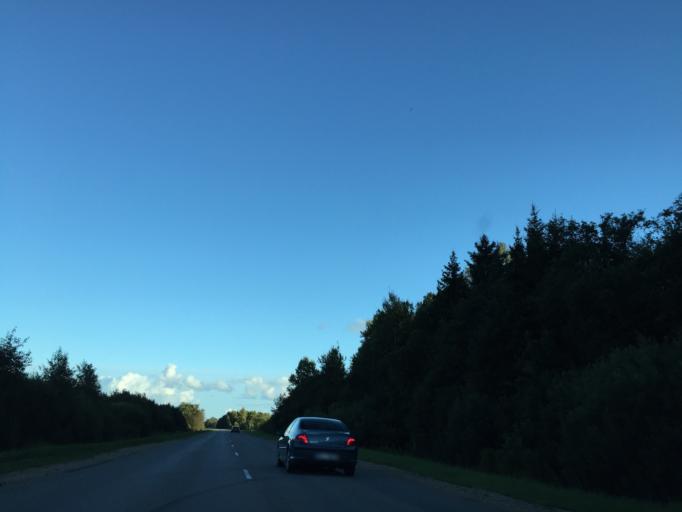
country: LV
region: Kuldigas Rajons
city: Kuldiga
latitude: 56.9501
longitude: 22.0134
